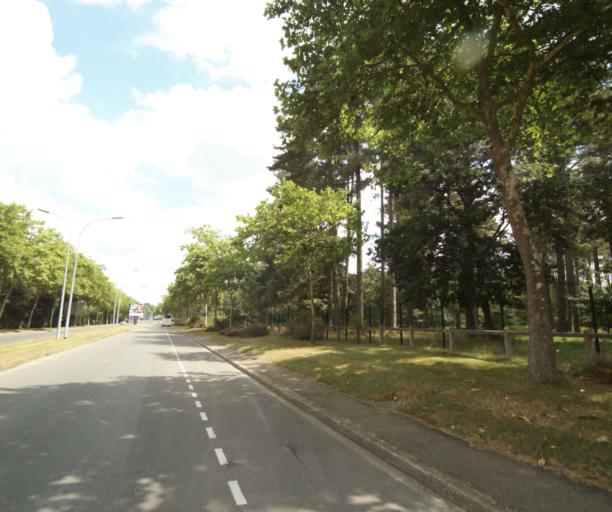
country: FR
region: Centre
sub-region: Departement du Loiret
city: Saint-Cyr-en-Val
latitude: 47.8341
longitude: 1.9403
